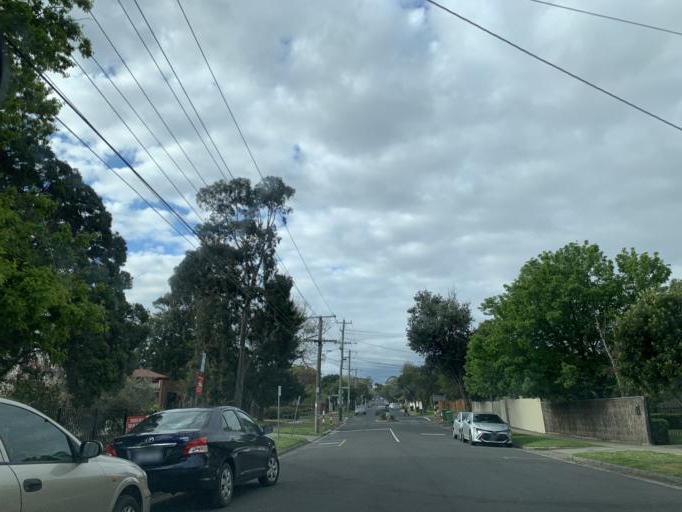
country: AU
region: Victoria
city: Beaumaris
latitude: -37.9855
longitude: 145.0379
